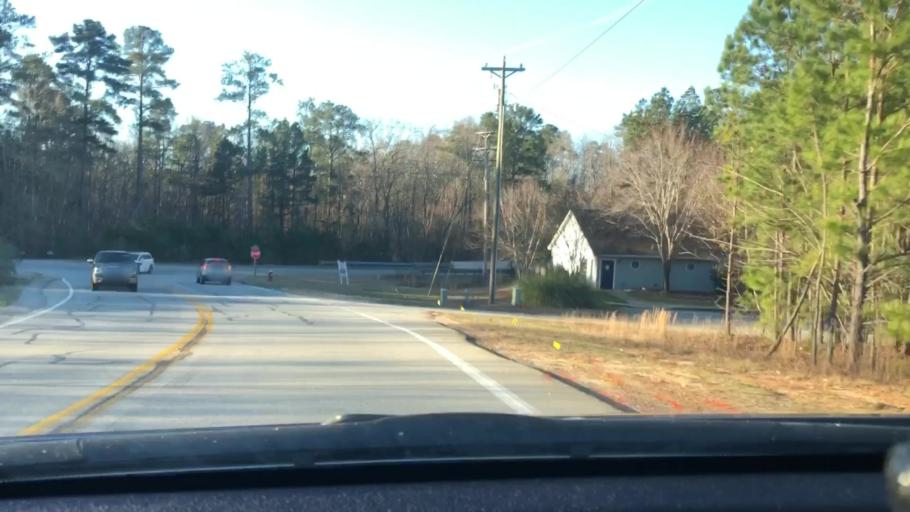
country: US
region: South Carolina
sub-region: Lexington County
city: Irmo
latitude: 34.0546
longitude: -81.1854
